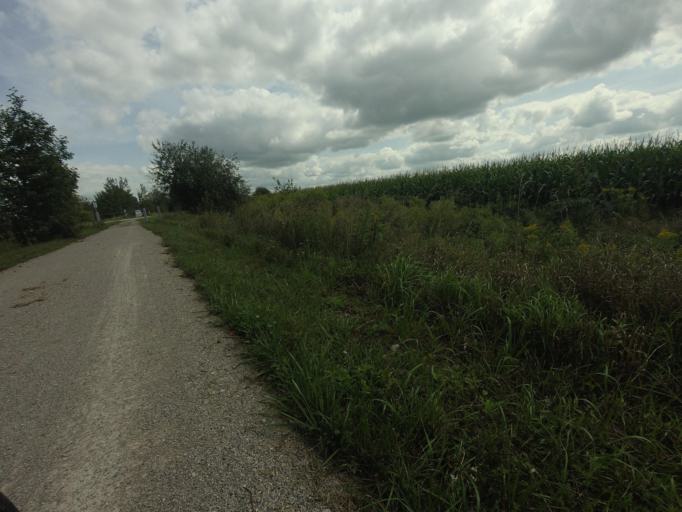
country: CA
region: Ontario
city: North Perth
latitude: 43.5627
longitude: -81.0044
